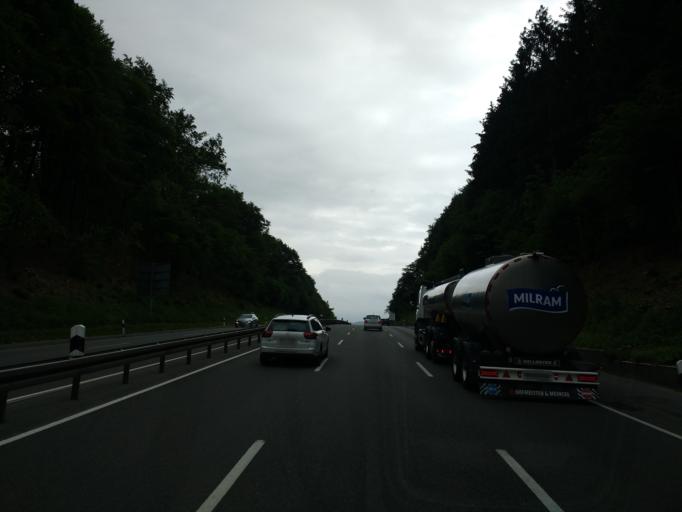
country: DE
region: Lower Saxony
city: Georgsmarienhutte
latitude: 52.2347
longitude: 8.0615
